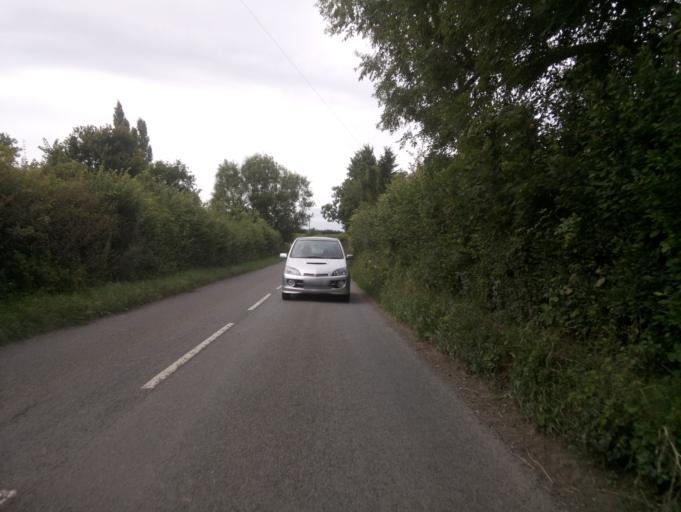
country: GB
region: England
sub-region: Somerset
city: Street
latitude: 51.1148
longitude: -2.7065
